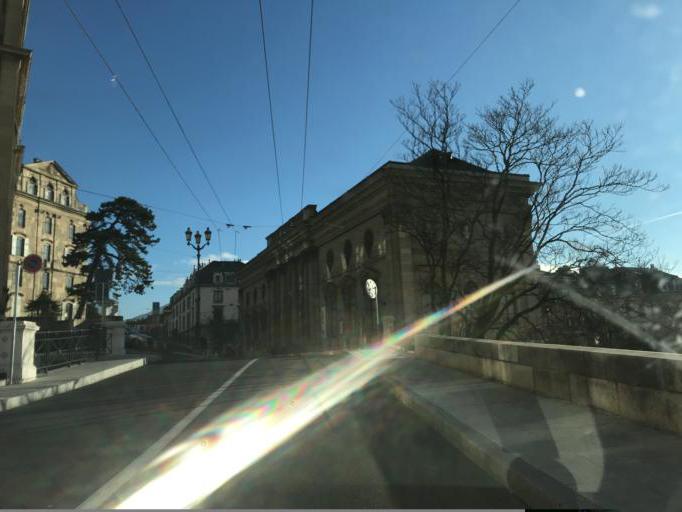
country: CH
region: Geneva
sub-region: Geneva
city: Geneve
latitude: 46.1992
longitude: 6.1475
